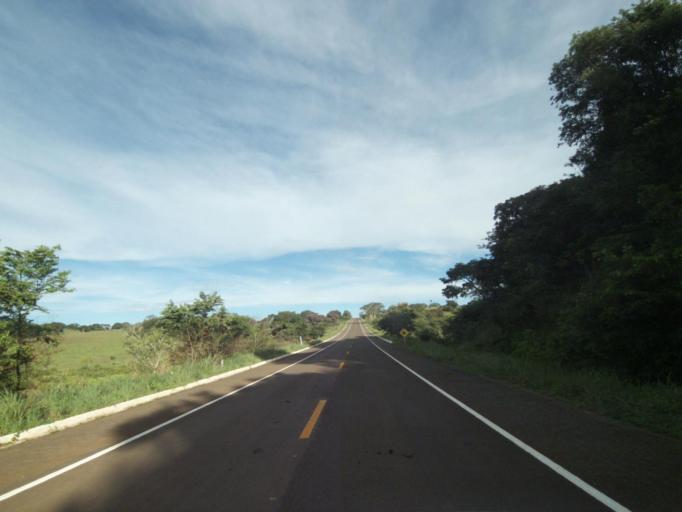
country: BR
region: Goias
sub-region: Jaragua
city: Jaragua
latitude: -15.8930
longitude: -49.5091
